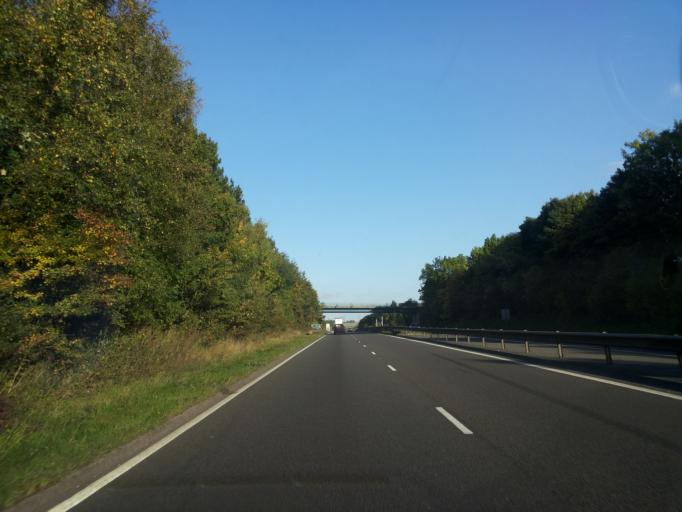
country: GB
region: England
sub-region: Derbyshire
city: Pilsley
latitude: 53.2008
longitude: -1.3481
